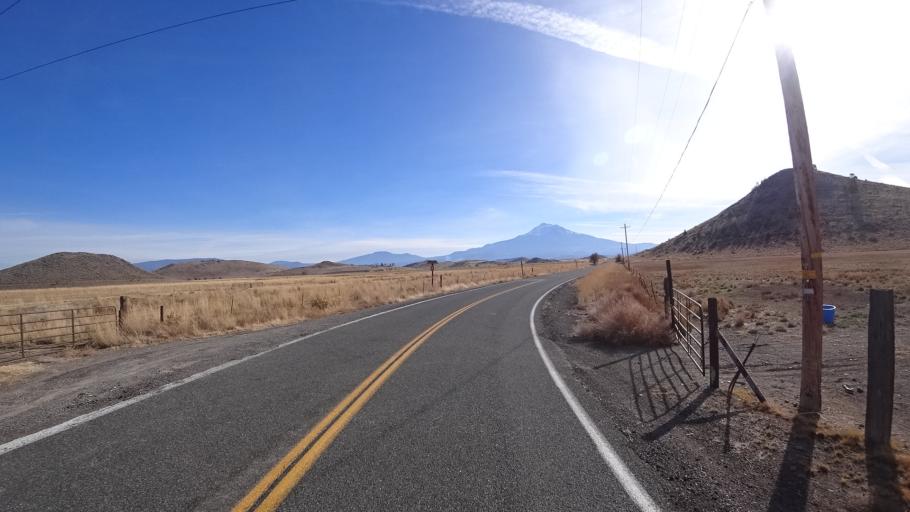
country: US
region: California
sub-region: Siskiyou County
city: Weed
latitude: 41.5381
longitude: -122.5236
